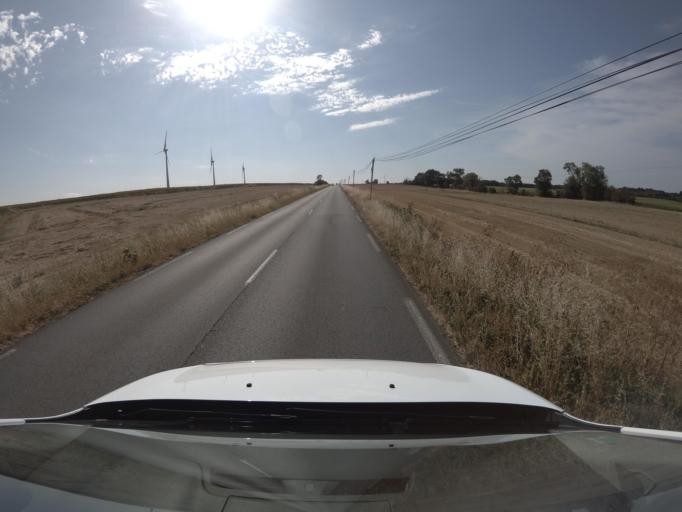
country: FR
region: Poitou-Charentes
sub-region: Departement des Deux-Sevres
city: Mauze-Thouarsais
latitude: 46.9985
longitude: -0.2706
